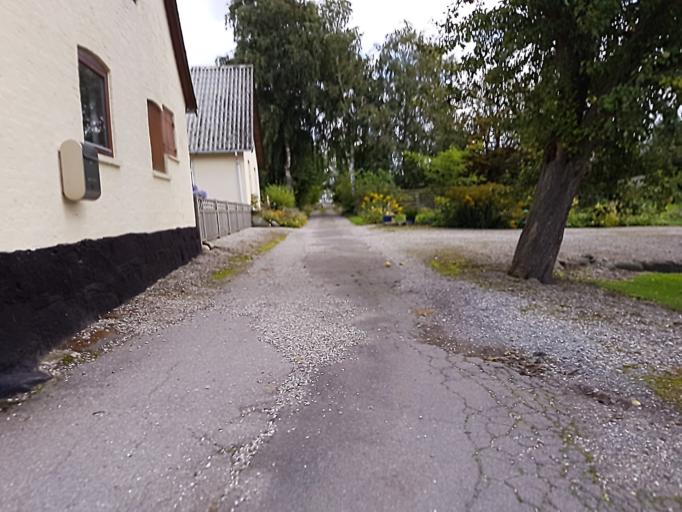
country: DK
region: Zealand
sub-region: Roskilde Kommune
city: Gundsomagle
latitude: 55.7493
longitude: 12.1332
